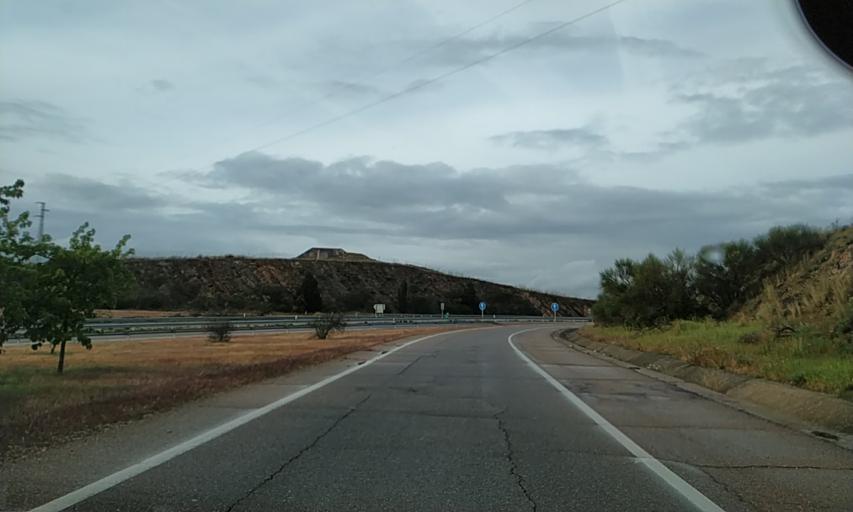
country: ES
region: Extremadura
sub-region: Provincia de Badajoz
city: Badajoz
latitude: 38.9088
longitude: -6.9940
